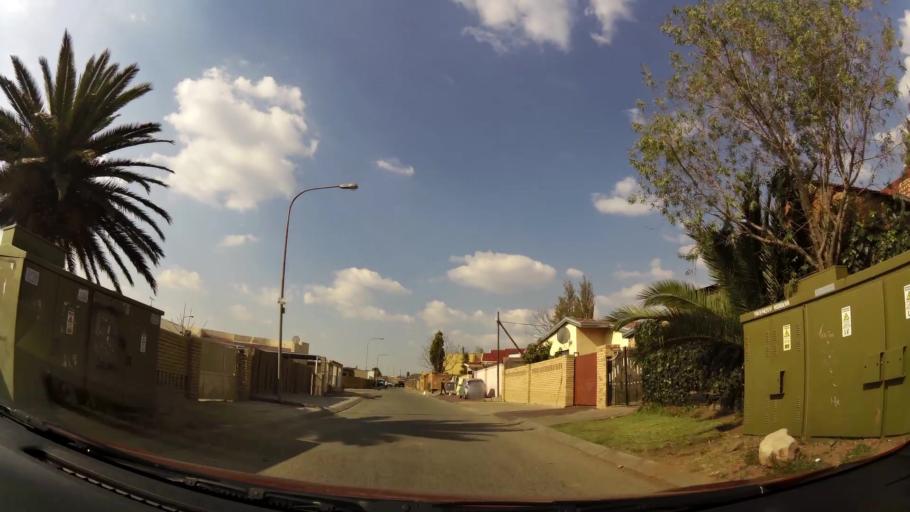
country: ZA
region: Gauteng
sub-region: City of Johannesburg Metropolitan Municipality
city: Soweto
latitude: -26.2354
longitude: 27.9446
